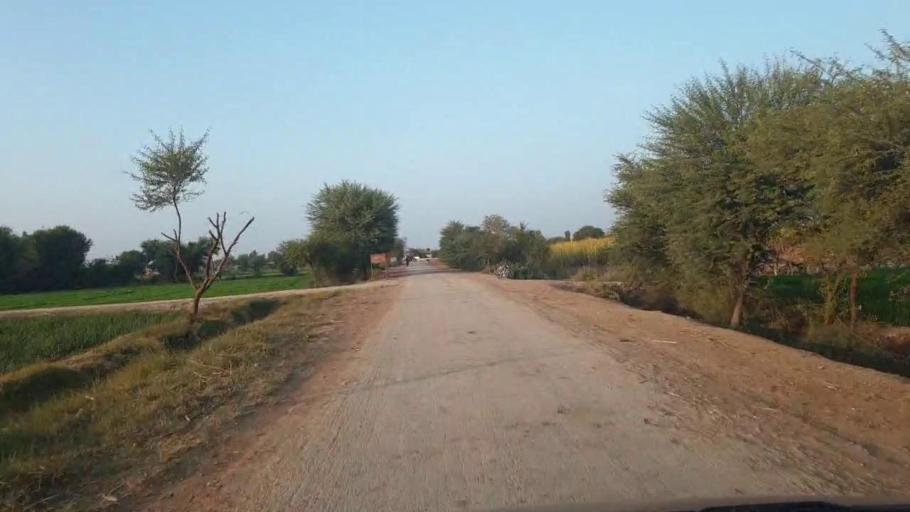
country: PK
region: Sindh
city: Berani
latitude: 25.8363
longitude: 68.7447
